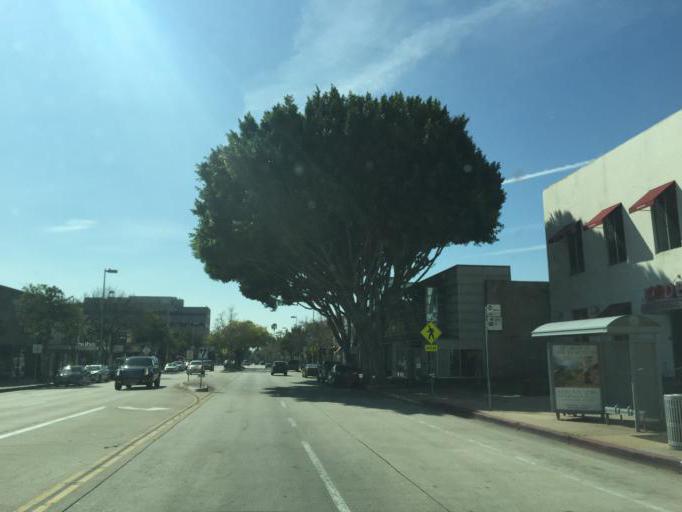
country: US
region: California
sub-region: Los Angeles County
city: Pasadena
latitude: 34.1378
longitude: -118.1323
